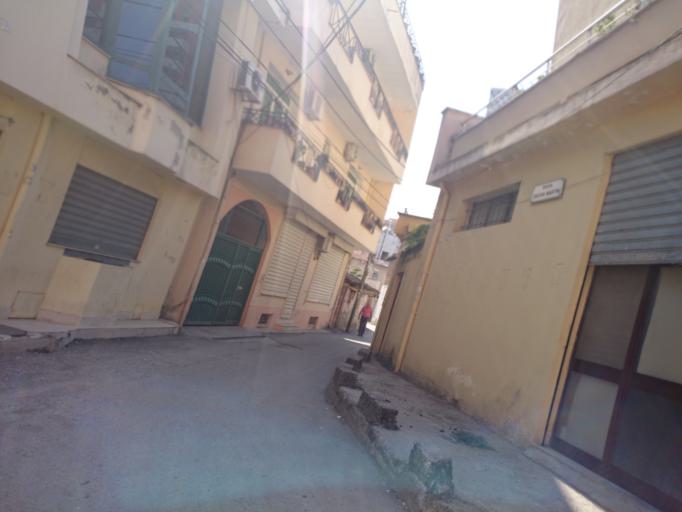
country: AL
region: Tirane
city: Tirana
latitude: 41.3281
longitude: 19.8240
